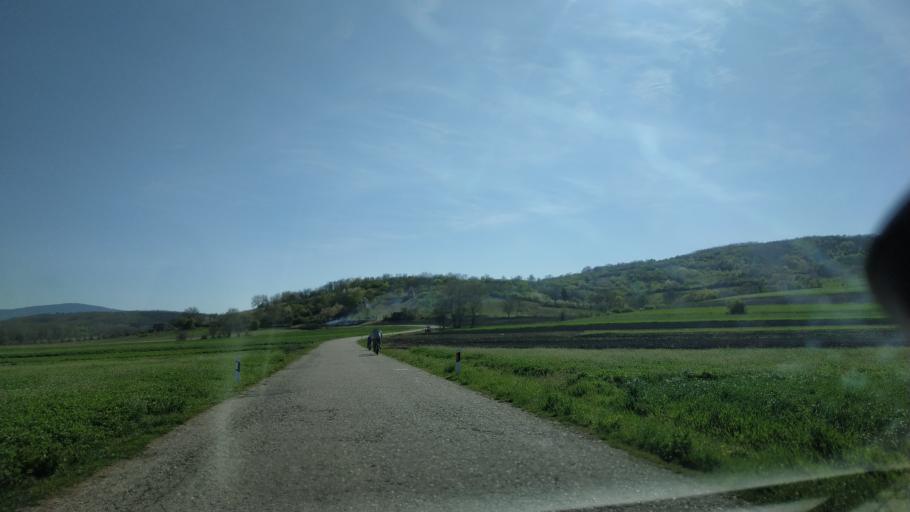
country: RS
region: Central Serbia
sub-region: Nisavski Okrug
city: Aleksinac
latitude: 43.5009
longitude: 21.6774
